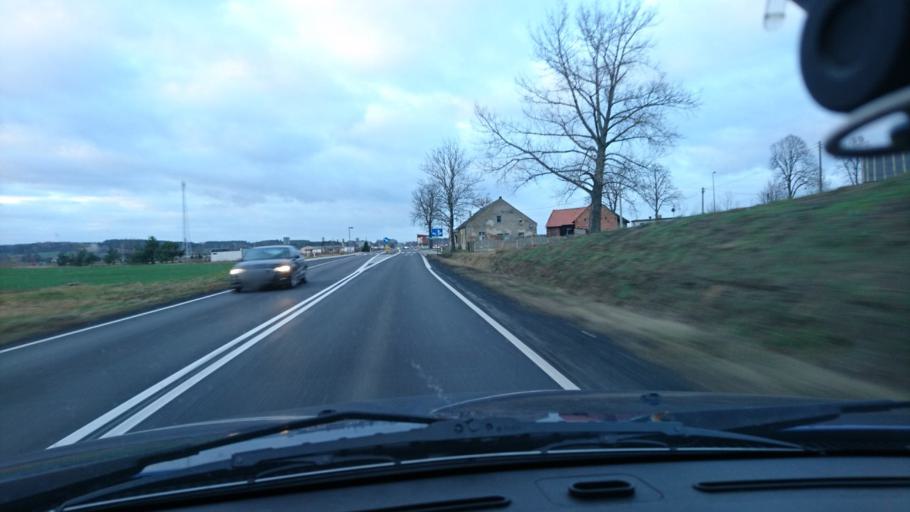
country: PL
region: Greater Poland Voivodeship
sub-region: Powiat ostrzeszowski
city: Ostrzeszow
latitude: 51.3861
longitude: 17.9488
